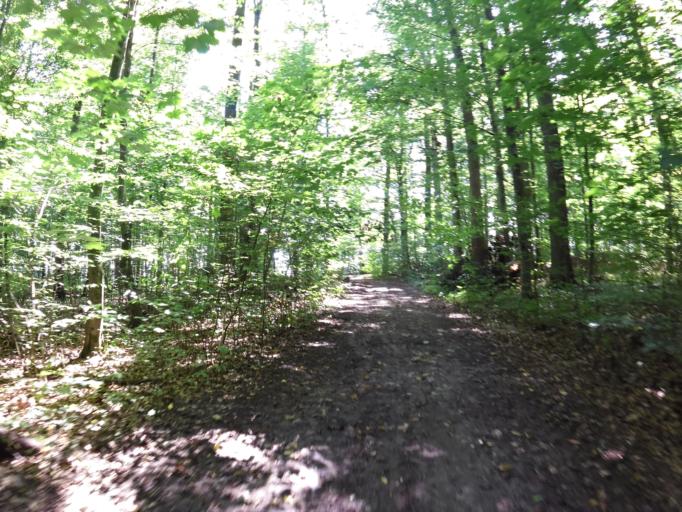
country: DE
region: Bavaria
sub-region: Regierungsbezirk Unterfranken
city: Veitshochheim
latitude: 49.8530
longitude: 9.8834
